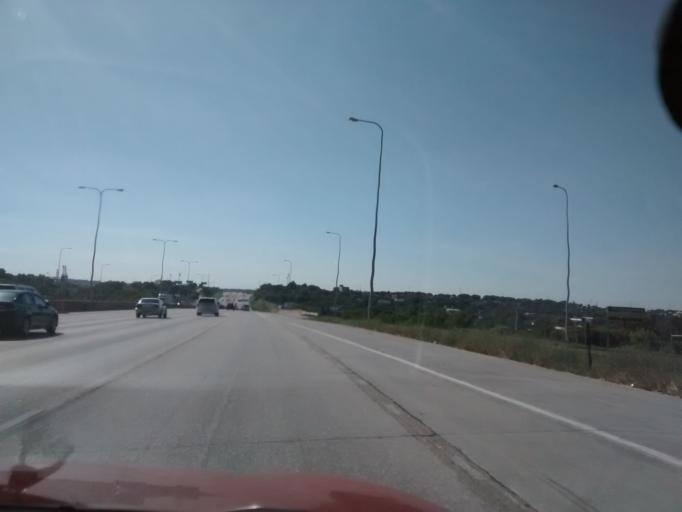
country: US
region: Nebraska
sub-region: Douglas County
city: Ralston
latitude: 41.2238
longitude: -96.0024
